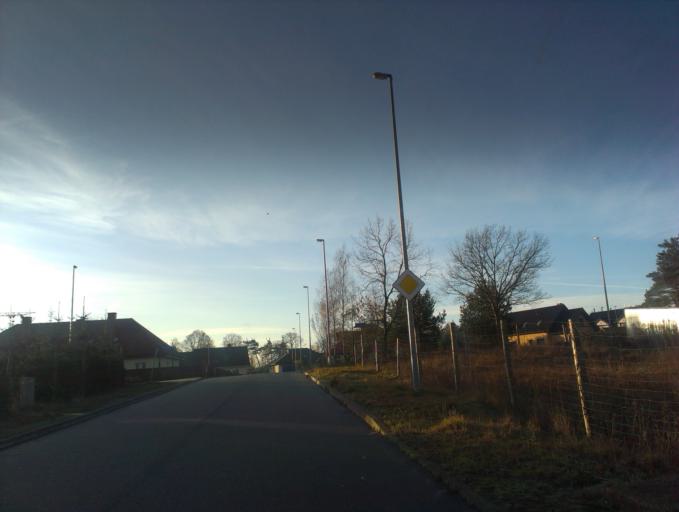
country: PL
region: West Pomeranian Voivodeship
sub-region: Powiat szczecinecki
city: Szczecinek
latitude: 53.7185
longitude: 16.6583
